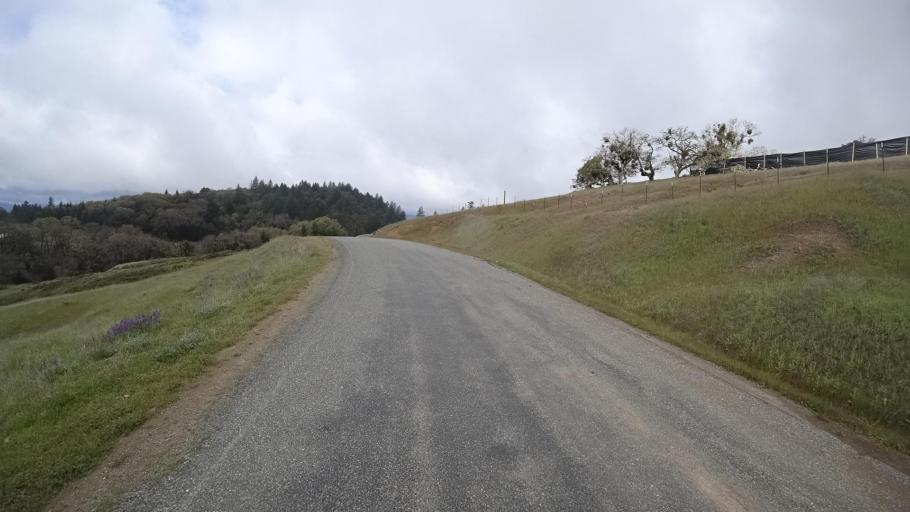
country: US
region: California
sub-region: Humboldt County
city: Redway
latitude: 40.1562
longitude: -123.5426
